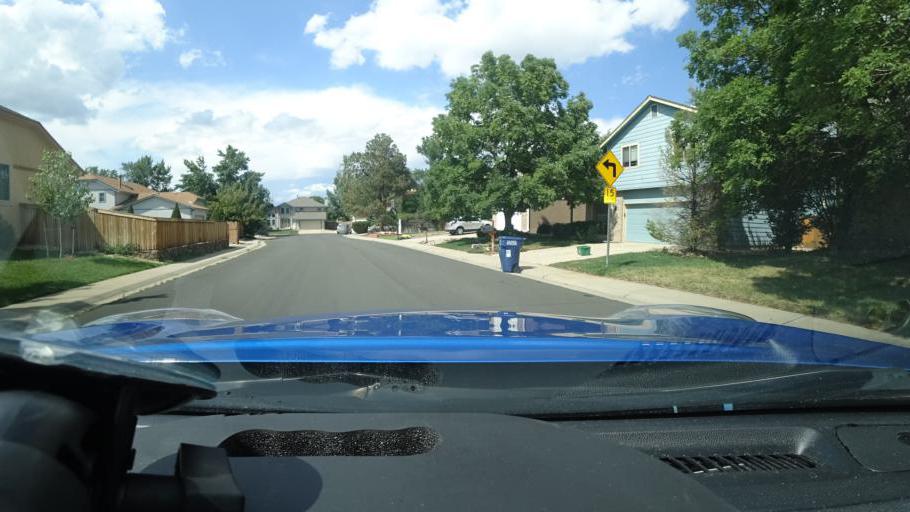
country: US
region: Colorado
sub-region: Adams County
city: Aurora
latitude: 39.6774
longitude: -104.8548
